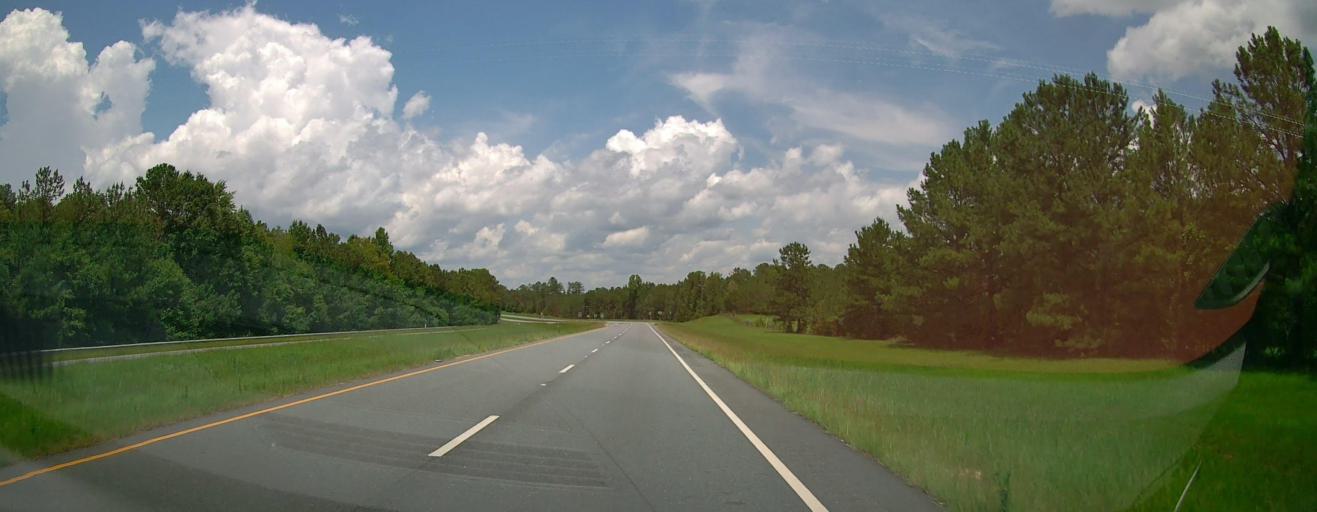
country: US
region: Georgia
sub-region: Upson County
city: Thomaston
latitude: 32.7595
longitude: -84.2441
